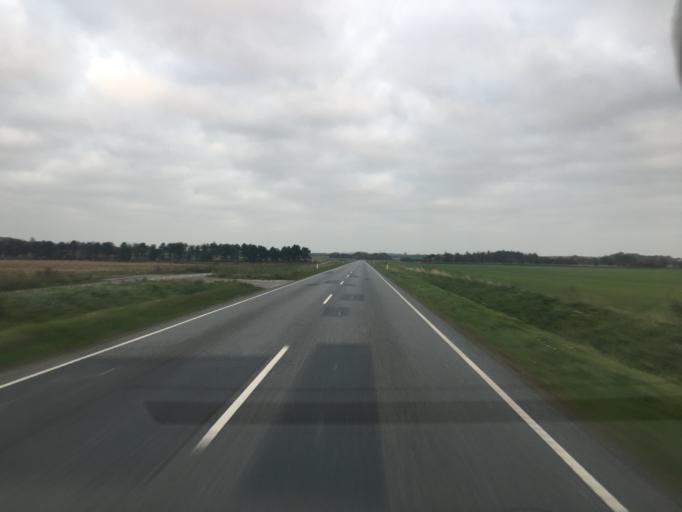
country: DE
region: Schleswig-Holstein
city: Aventoft
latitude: 54.9495
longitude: 8.8147
